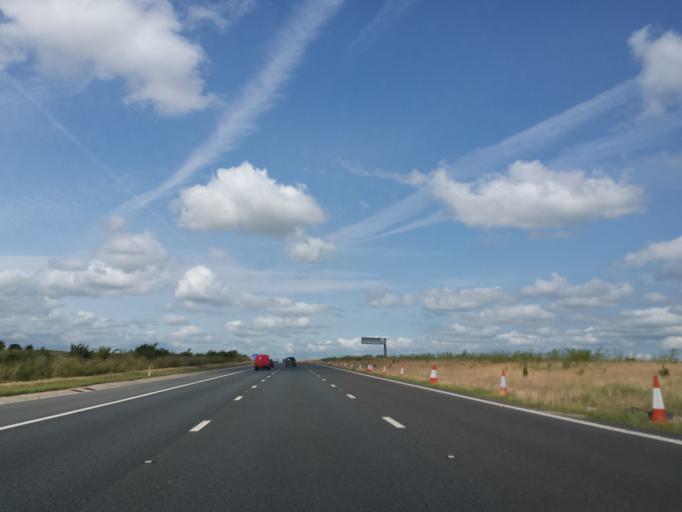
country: GB
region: England
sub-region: North Yorkshire
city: Ripon
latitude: 54.1703
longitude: -1.4517
